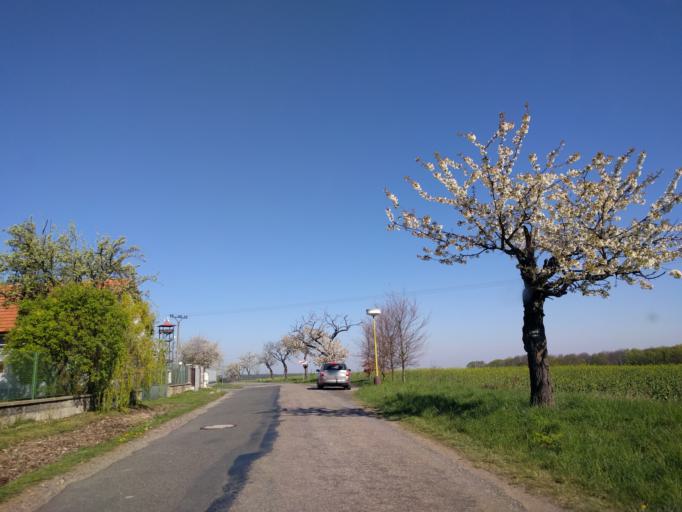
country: CZ
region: Central Bohemia
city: Mukarov
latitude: 49.9884
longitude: 14.7853
